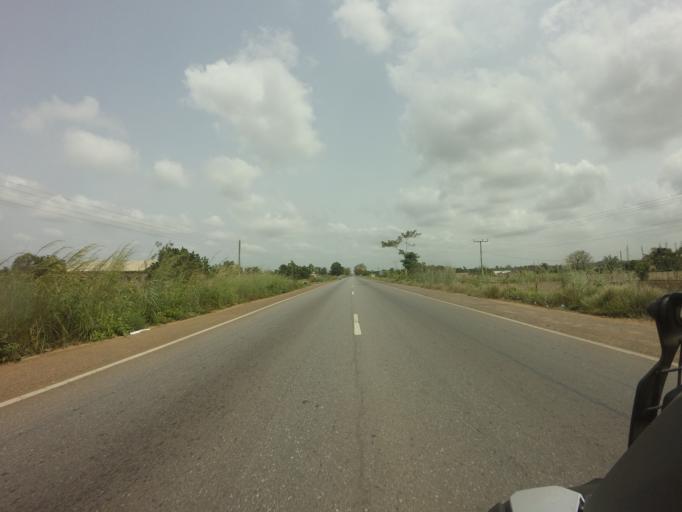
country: GH
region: Volta
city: Anloga
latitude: 5.9067
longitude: 0.5225
